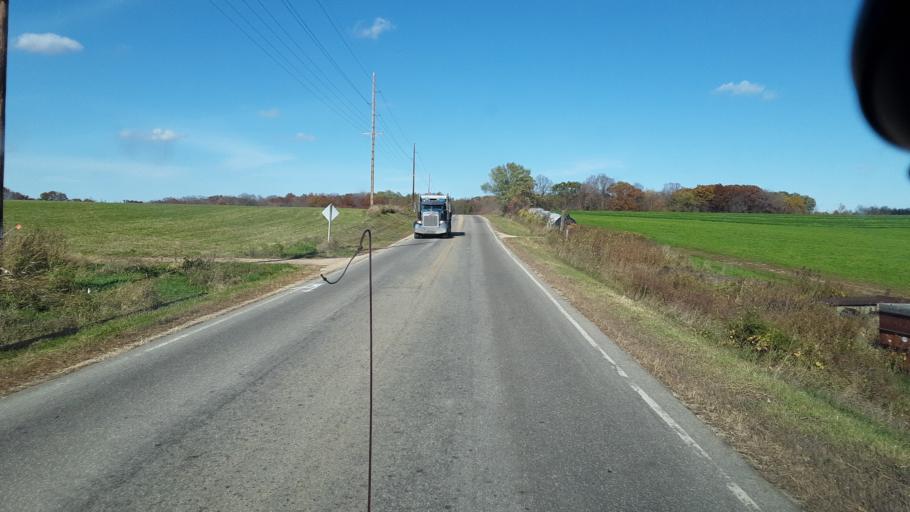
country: US
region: Wisconsin
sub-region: Vernon County
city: Hillsboro
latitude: 43.6686
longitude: -90.4586
